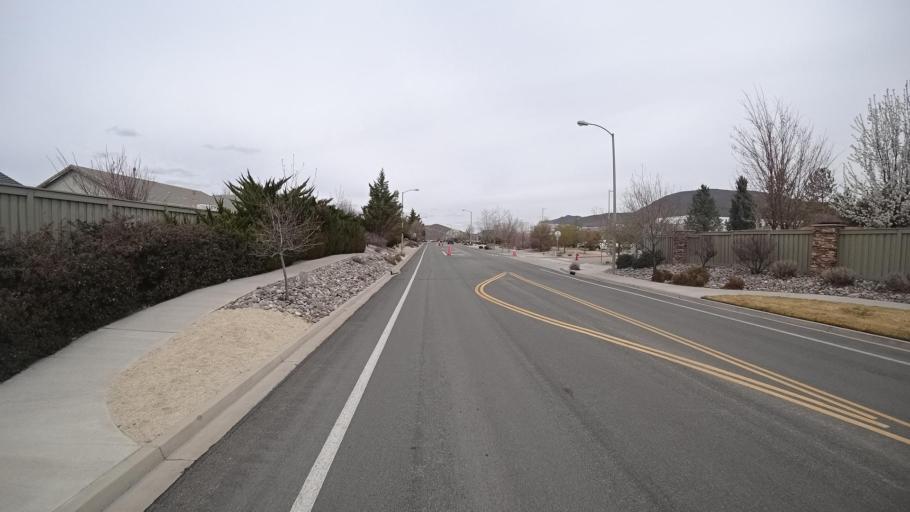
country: US
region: Nevada
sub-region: Washoe County
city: Sparks
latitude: 39.4470
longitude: -119.7363
